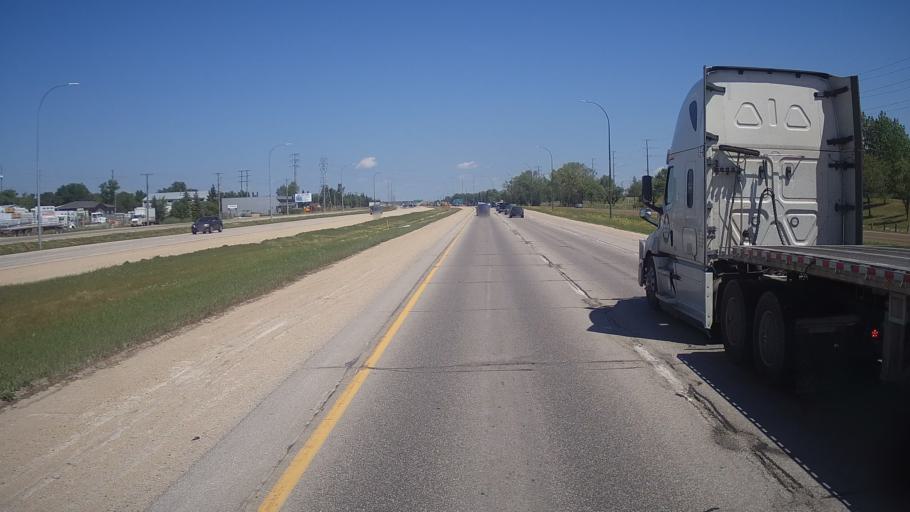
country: CA
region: Manitoba
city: Winnipeg
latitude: 49.9331
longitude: -97.0425
